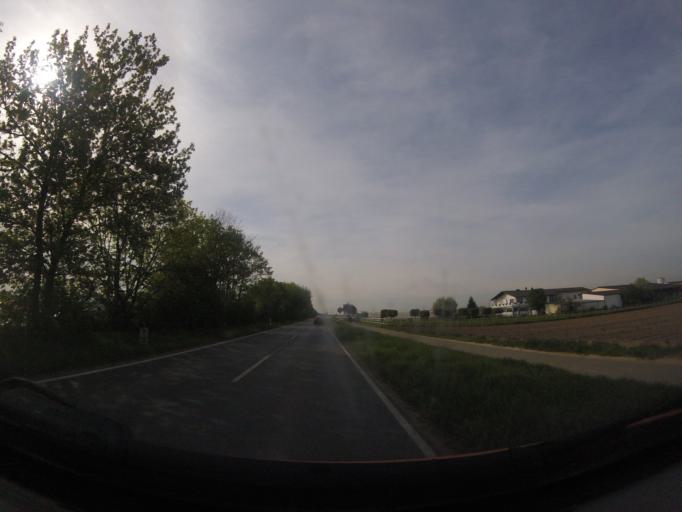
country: DE
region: Hesse
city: Griesheim
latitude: 49.8483
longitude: 8.5580
